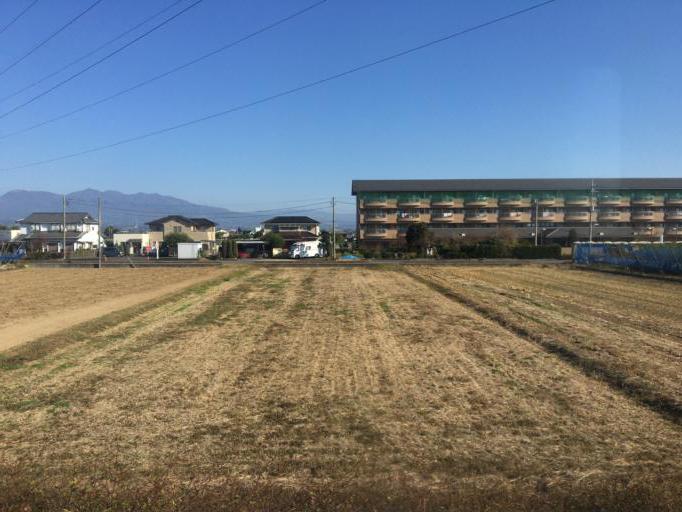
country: JP
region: Gunma
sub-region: Sawa-gun
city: Tamamura
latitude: 36.3620
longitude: 139.1253
